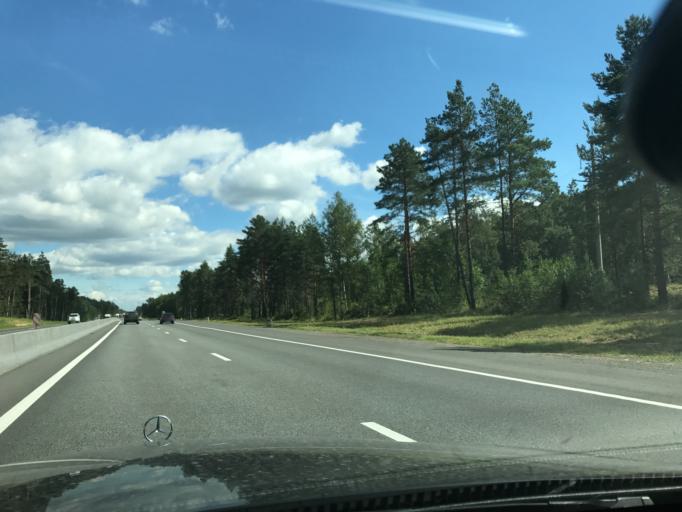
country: RU
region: Nizjnij Novgorod
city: Yuganets
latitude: 56.2879
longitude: 43.2293
